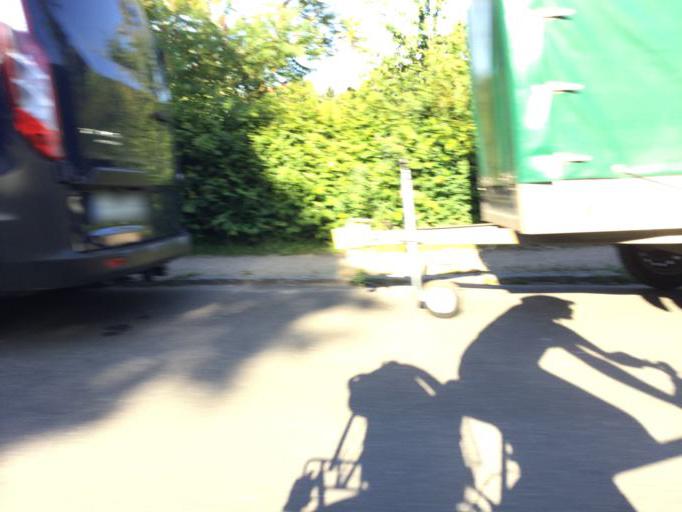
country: DE
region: Hamburg
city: Langenhorn
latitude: 53.6571
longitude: 10.0175
